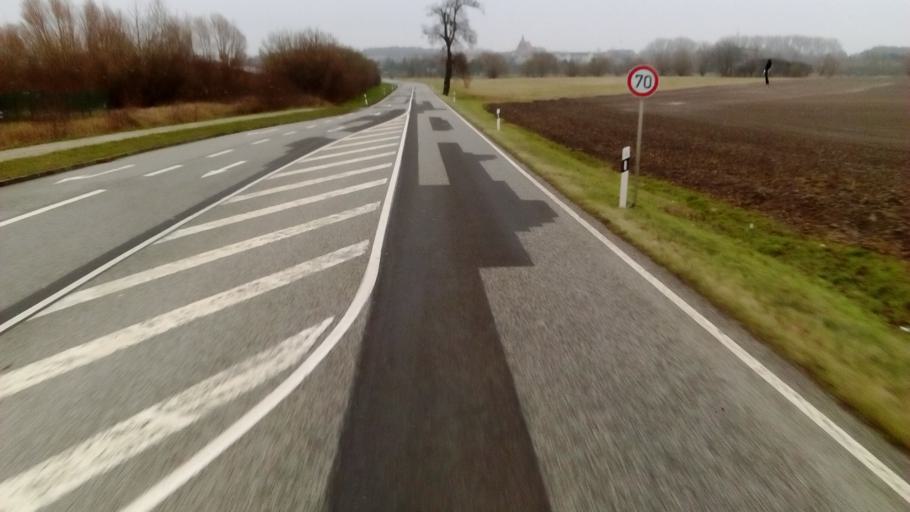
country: DE
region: Mecklenburg-Vorpommern
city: Strasburg
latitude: 53.4985
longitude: 13.7306
